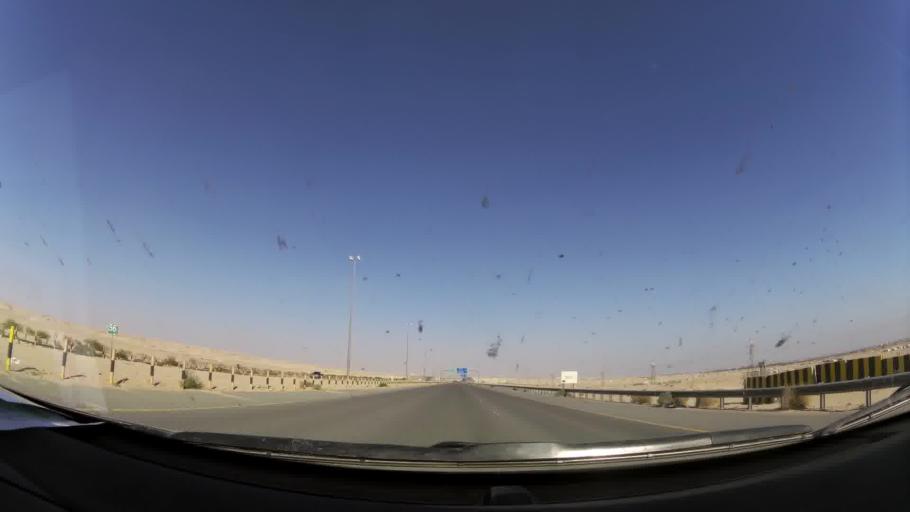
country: KW
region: Muhafazat al Jahra'
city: Al Jahra'
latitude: 29.4001
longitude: 47.6895
